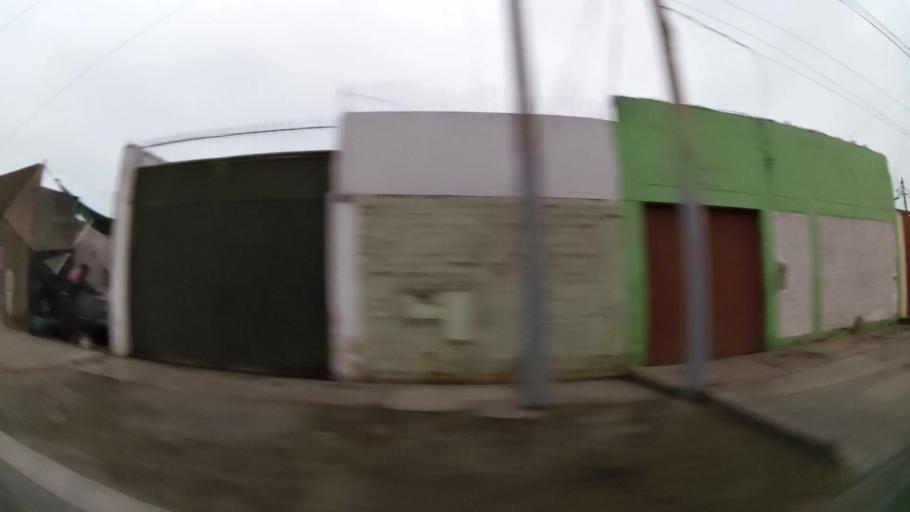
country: PE
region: Callao
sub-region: Callao
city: Callao
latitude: -12.0786
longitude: -77.1053
